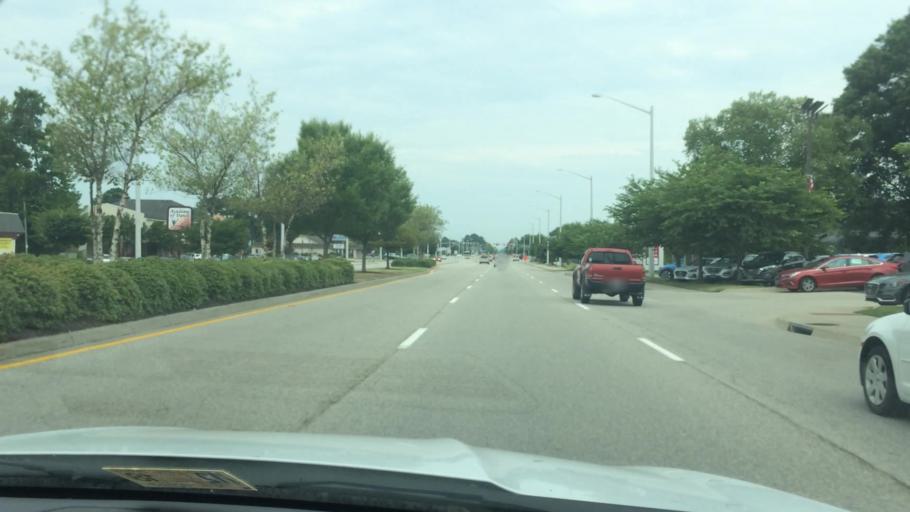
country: US
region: Virginia
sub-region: York County
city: Yorktown
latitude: 37.1457
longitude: -76.5255
